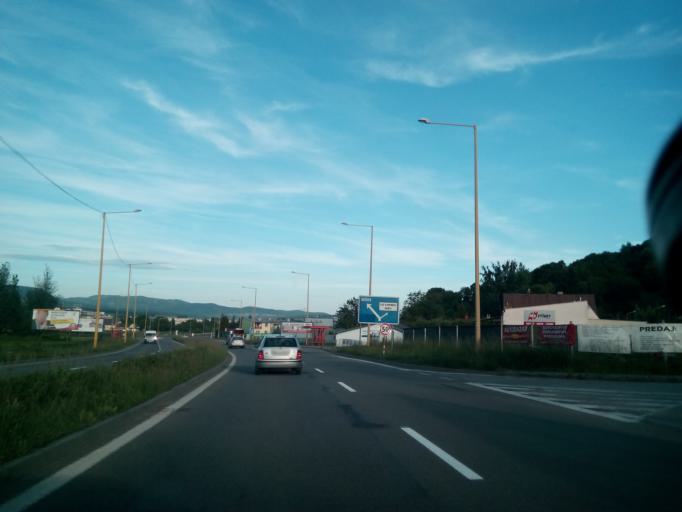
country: SK
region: Presovsky
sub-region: Okres Presov
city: Presov
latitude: 48.9837
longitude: 21.2320
